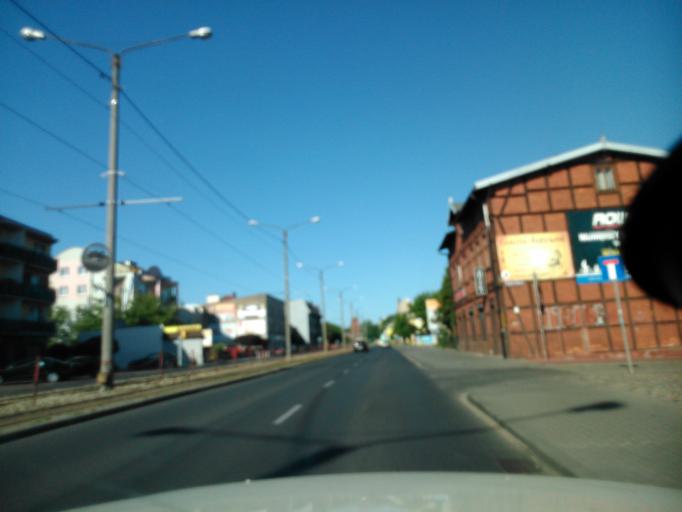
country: PL
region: Kujawsko-Pomorskie
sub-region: Torun
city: Torun
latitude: 53.0156
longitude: 18.6321
